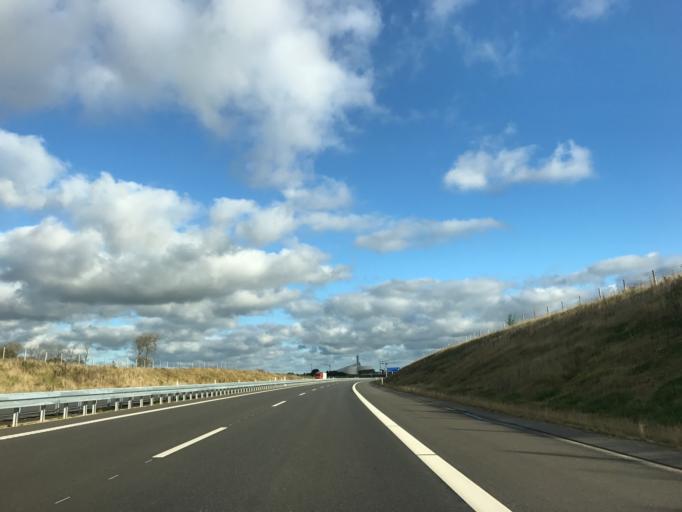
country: DK
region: Central Jutland
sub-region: Silkeborg Kommune
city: Silkeborg
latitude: 56.2041
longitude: 9.5390
